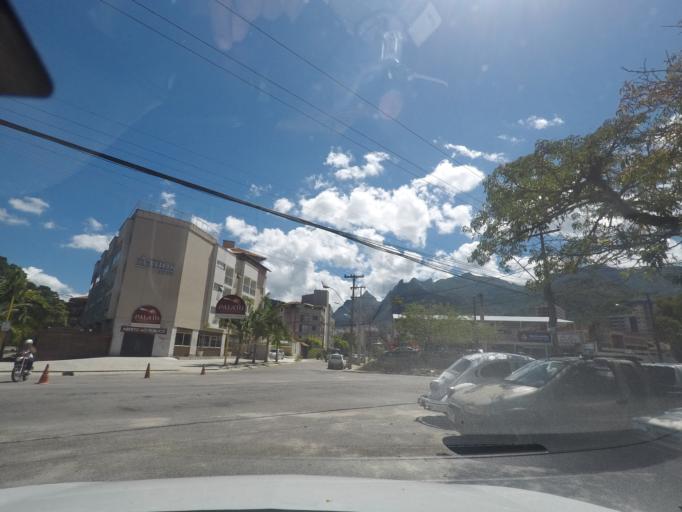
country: BR
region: Rio de Janeiro
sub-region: Teresopolis
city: Teresopolis
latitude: -22.4340
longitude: -42.9749
